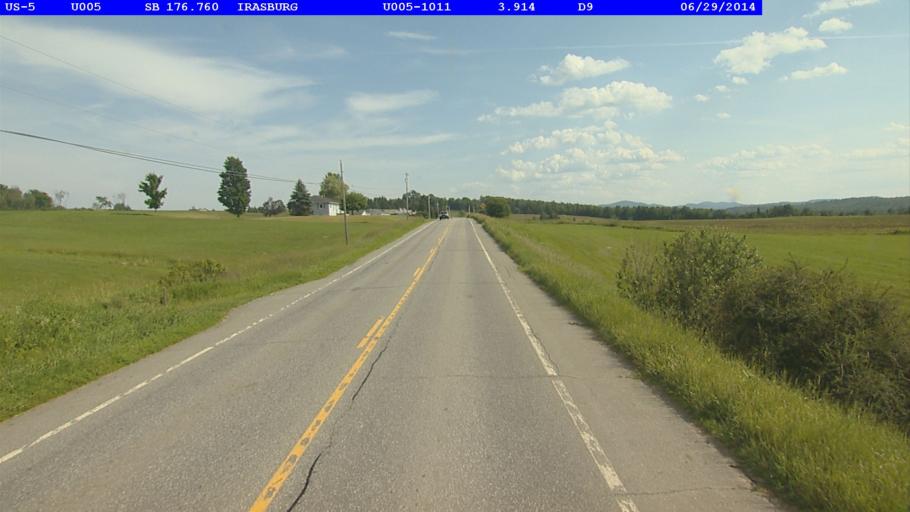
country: US
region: Vermont
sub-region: Orleans County
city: Newport
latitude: 44.8482
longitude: -72.2626
